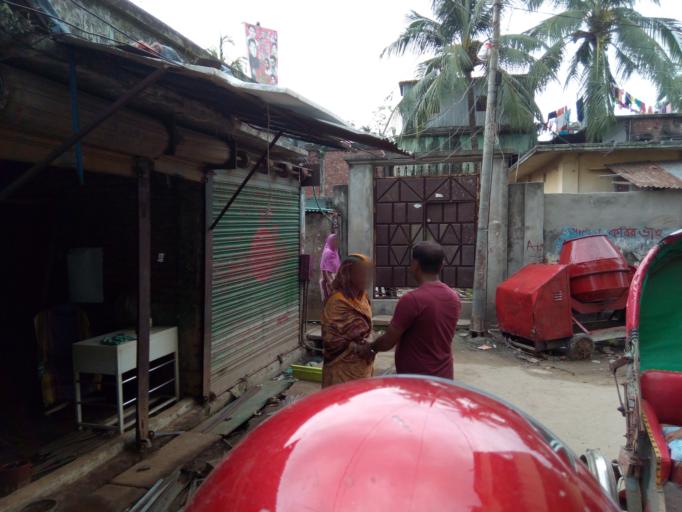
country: BD
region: Dhaka
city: Paltan
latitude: 23.7142
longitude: 90.4927
